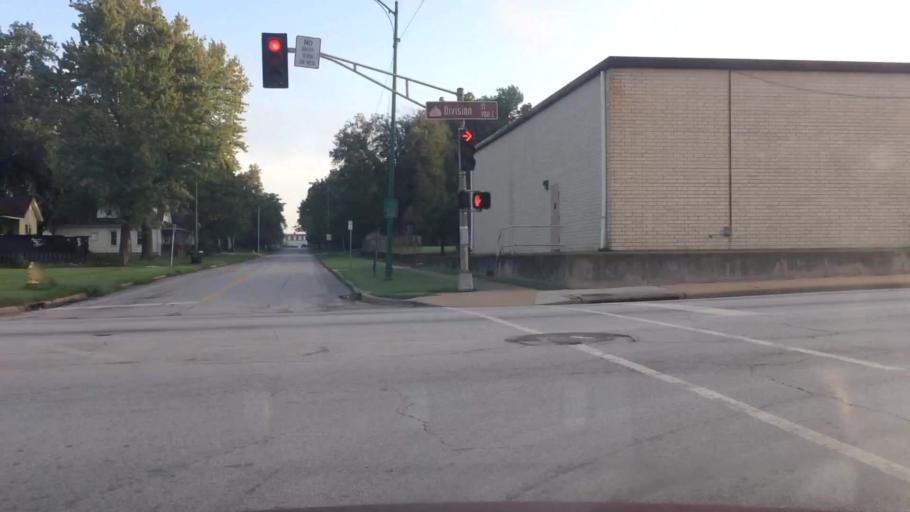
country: US
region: Missouri
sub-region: Greene County
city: Springfield
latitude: 37.2260
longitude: -93.2807
